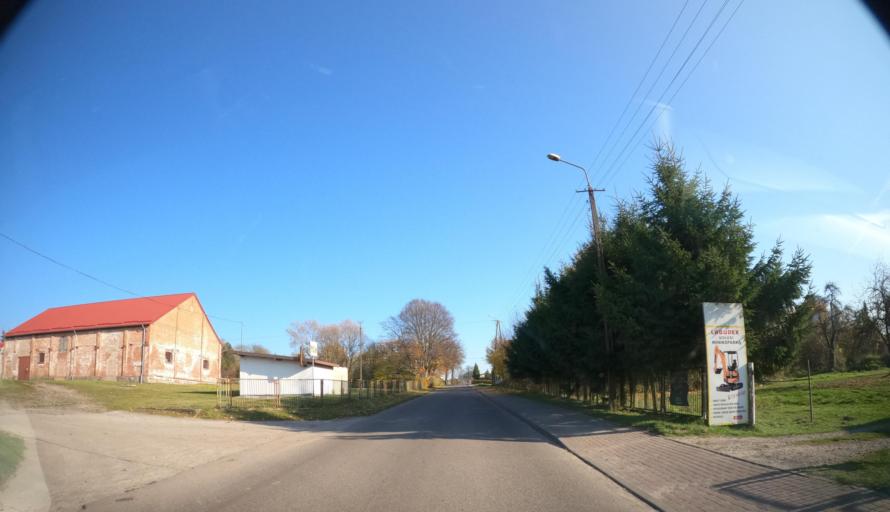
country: PL
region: Pomeranian Voivodeship
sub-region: Powiat slupski
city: Kepice
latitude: 54.2159
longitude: 16.8047
